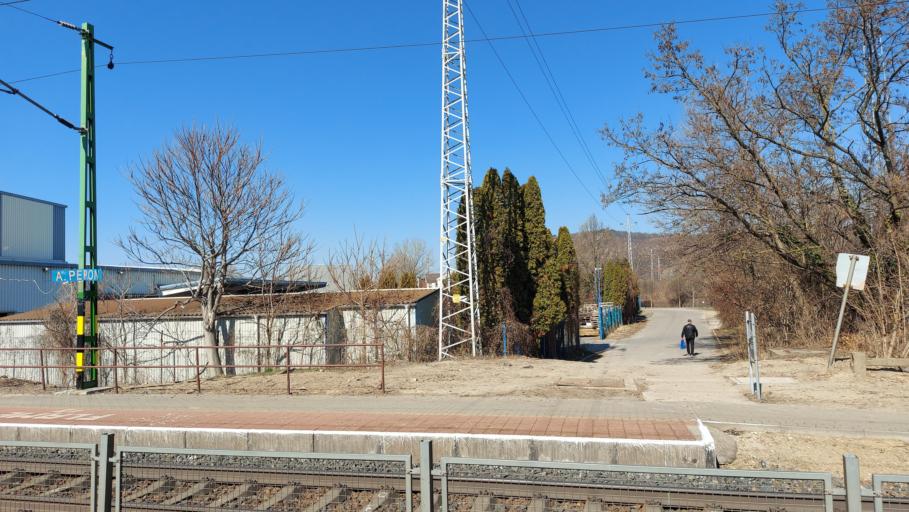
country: HU
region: Pest
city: Toeroekbalint
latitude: 47.4500
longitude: 18.9100
